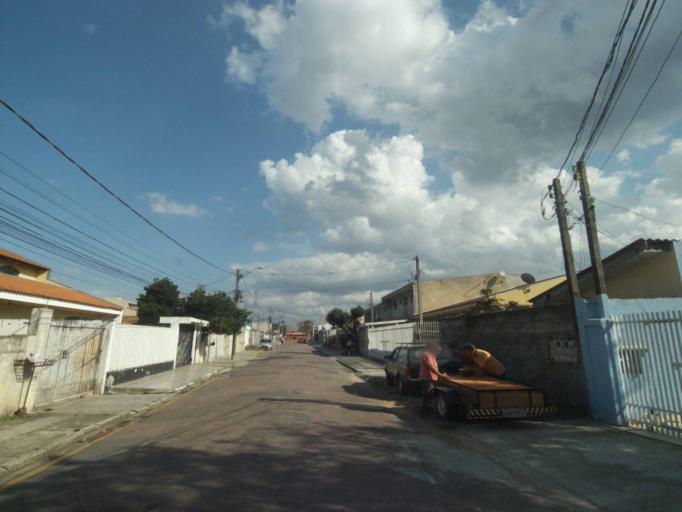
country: BR
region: Parana
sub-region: Sao Jose Dos Pinhais
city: Sao Jose dos Pinhais
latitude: -25.5326
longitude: -49.2699
